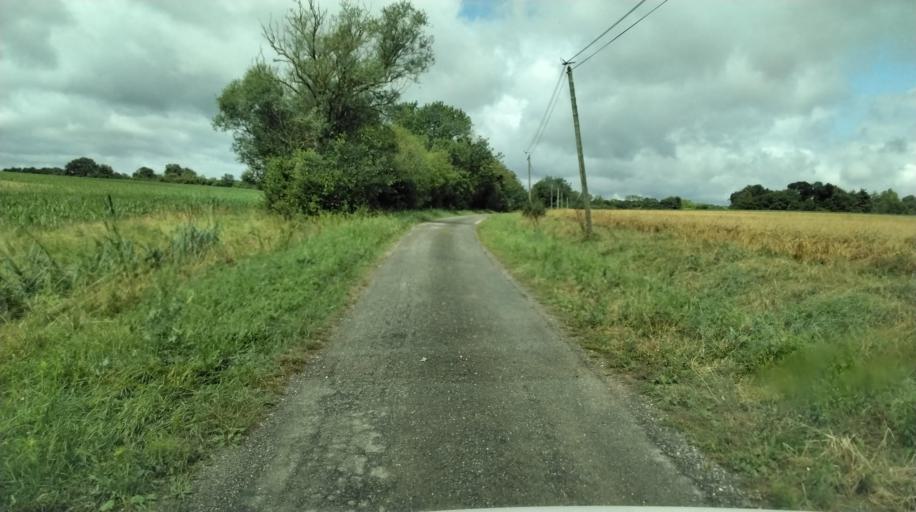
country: FR
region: Midi-Pyrenees
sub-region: Departement de la Haute-Garonne
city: Rieumes
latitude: 43.4230
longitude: 1.1520
